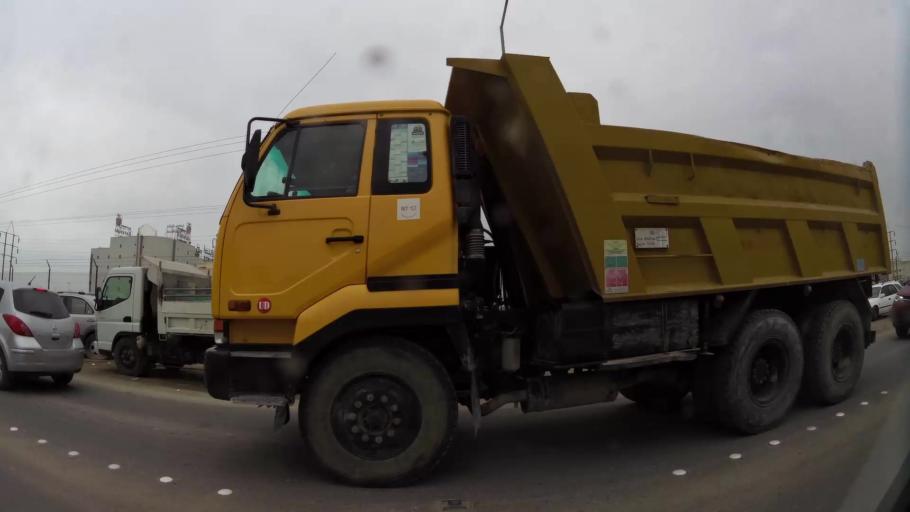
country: BH
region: Northern
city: Madinat `Isa
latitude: 26.1838
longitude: 50.5347
